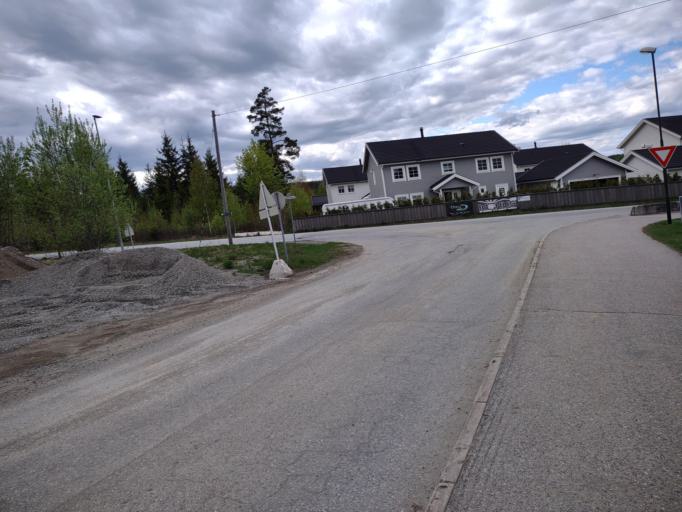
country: NO
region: Akershus
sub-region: Eidsvoll
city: Raholt
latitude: 60.2865
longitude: 11.1482
